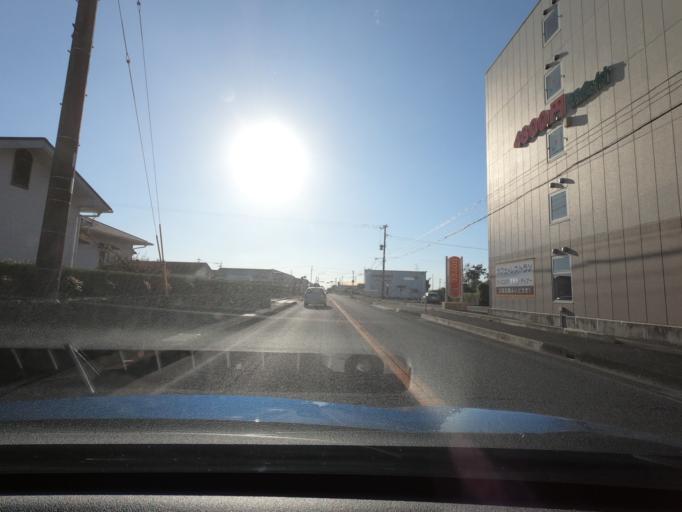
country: JP
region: Kagoshima
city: Izumi
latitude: 32.0979
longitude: 130.3038
